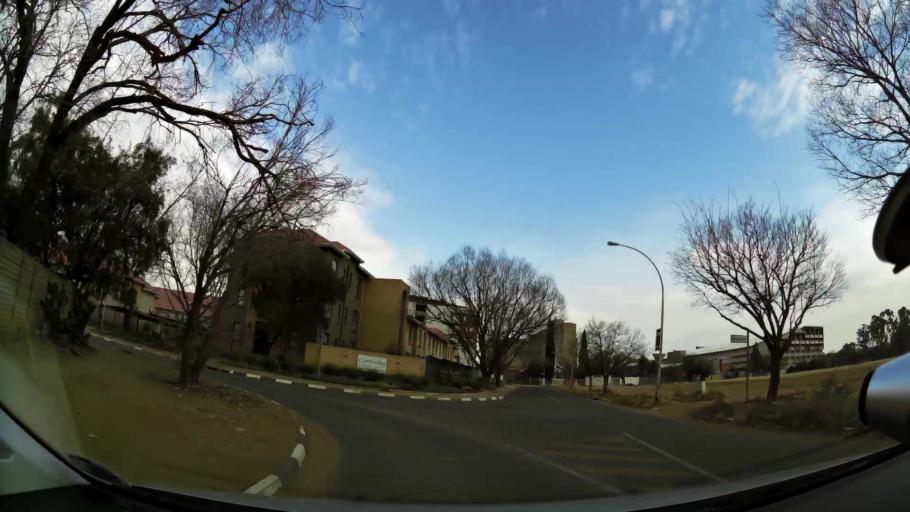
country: ZA
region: Orange Free State
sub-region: Mangaung Metropolitan Municipality
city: Bloemfontein
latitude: -29.1180
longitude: 26.1897
